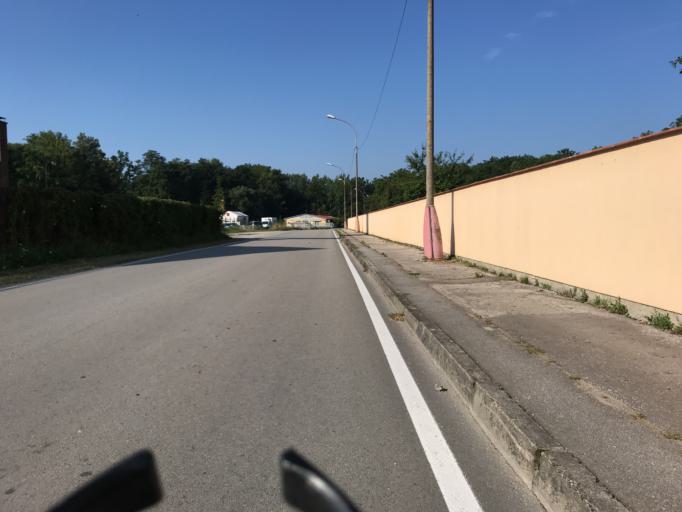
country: CZ
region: Jihocesky
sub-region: Okres Jindrichuv Hradec
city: Trebon
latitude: 48.9970
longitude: 14.7729
